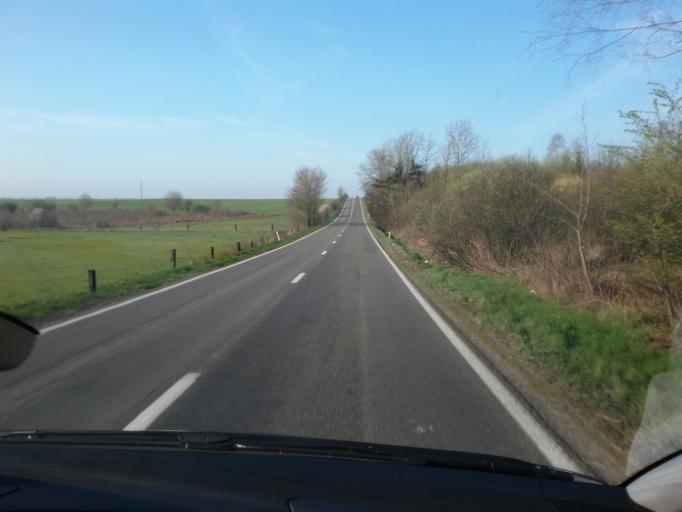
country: BE
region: Wallonia
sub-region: Province du Luxembourg
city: Etalle
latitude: 49.6948
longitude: 5.6157
